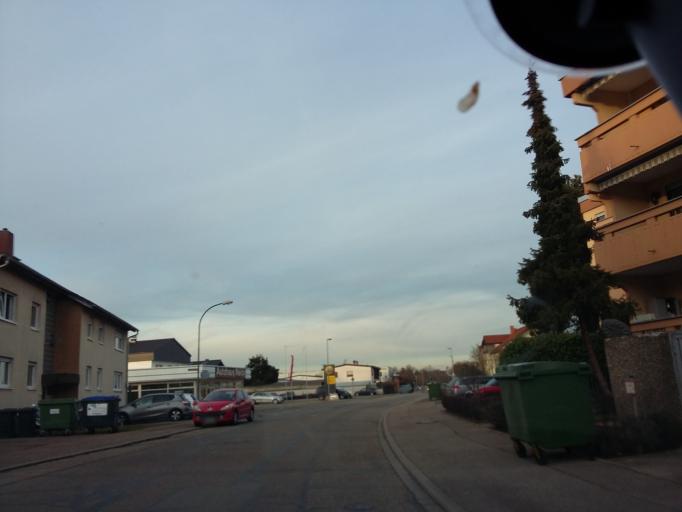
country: DE
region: Baden-Wuerttemberg
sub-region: Karlsruhe Region
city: Hockenheim
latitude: 49.3285
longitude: 8.5474
